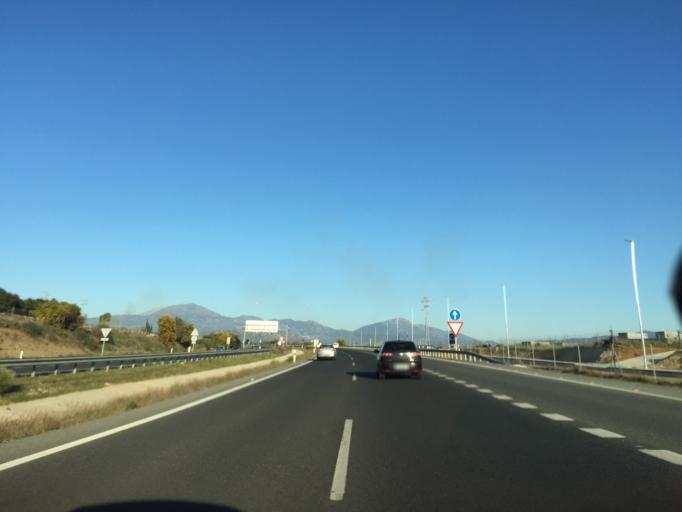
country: ES
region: Andalusia
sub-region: Provincia de Malaga
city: Cartama
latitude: 36.7190
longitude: -4.6686
